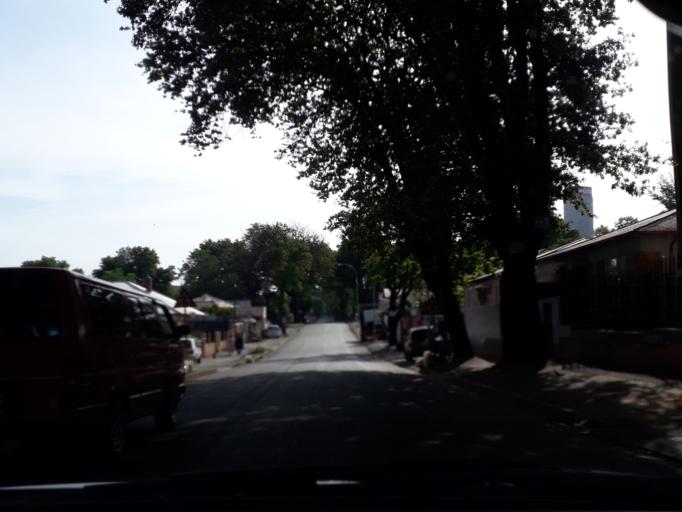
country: ZA
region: Gauteng
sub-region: City of Johannesburg Metropolitan Municipality
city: Johannesburg
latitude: -26.1901
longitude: 28.0690
